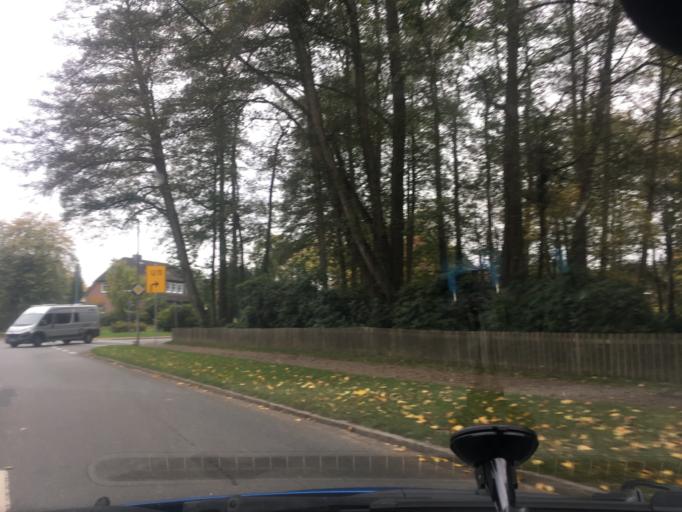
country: DE
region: Lower Saxony
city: Bispingen
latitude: 53.0964
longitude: 10.0272
